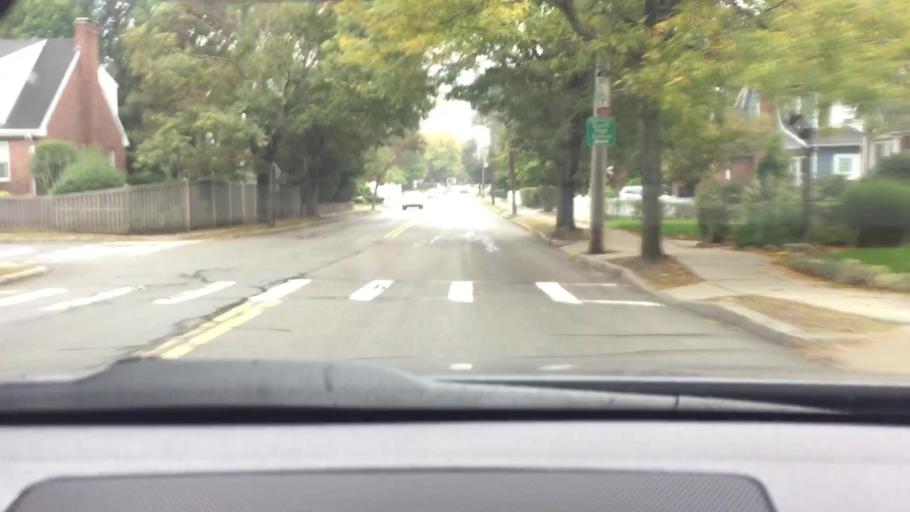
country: US
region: Massachusetts
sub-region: Middlesex County
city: Newton
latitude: 42.3164
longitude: -71.1950
